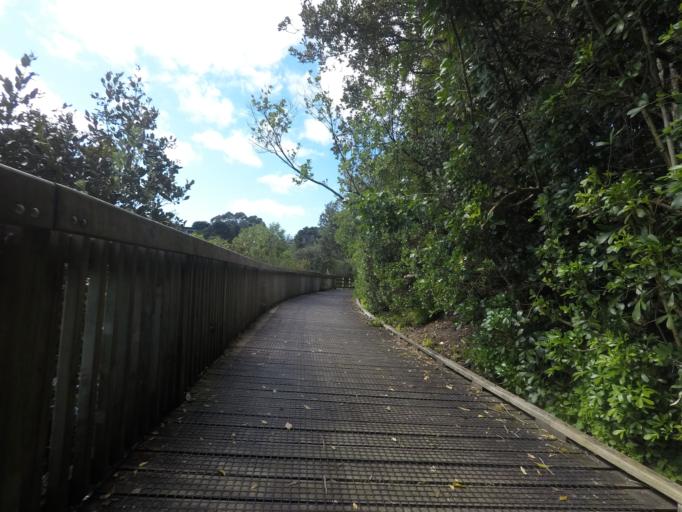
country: NZ
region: Auckland
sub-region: Auckland
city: Auckland
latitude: -36.8524
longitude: 174.7306
